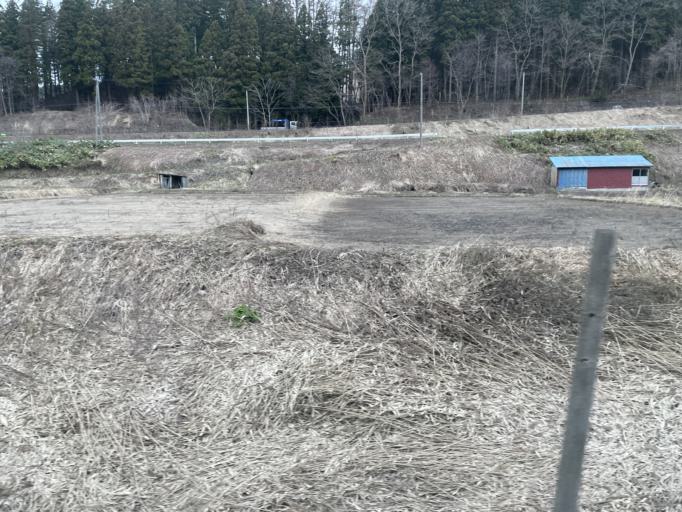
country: JP
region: Aomori
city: Namioka
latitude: 40.7787
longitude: 140.6198
